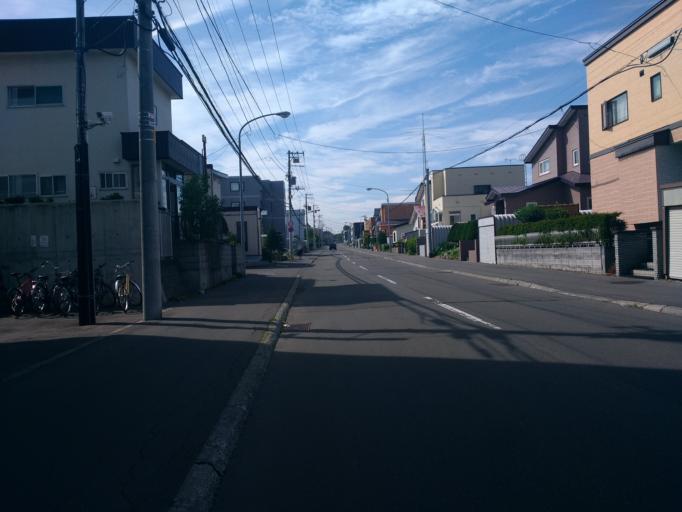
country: JP
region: Hokkaido
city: Ebetsu
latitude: 43.0708
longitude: 141.4978
